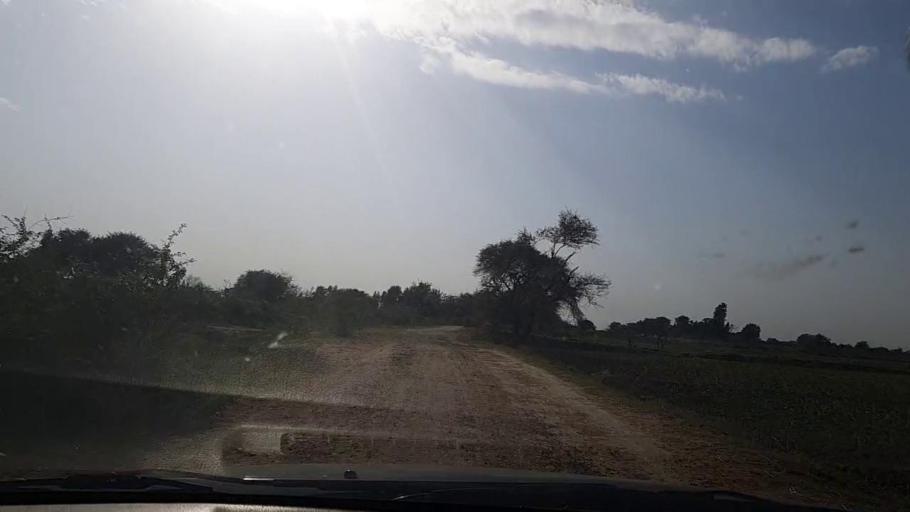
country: PK
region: Sindh
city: Mirpur Batoro
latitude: 24.5528
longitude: 68.1756
